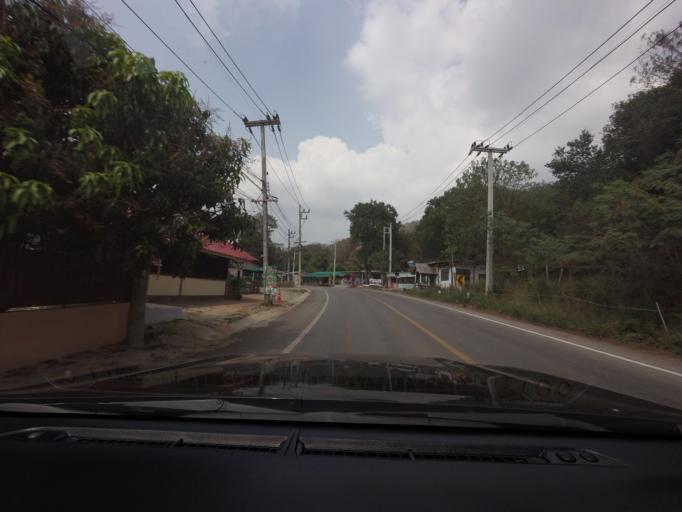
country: TH
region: Sara Buri
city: Muak Lek
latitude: 14.6215
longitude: 101.2125
